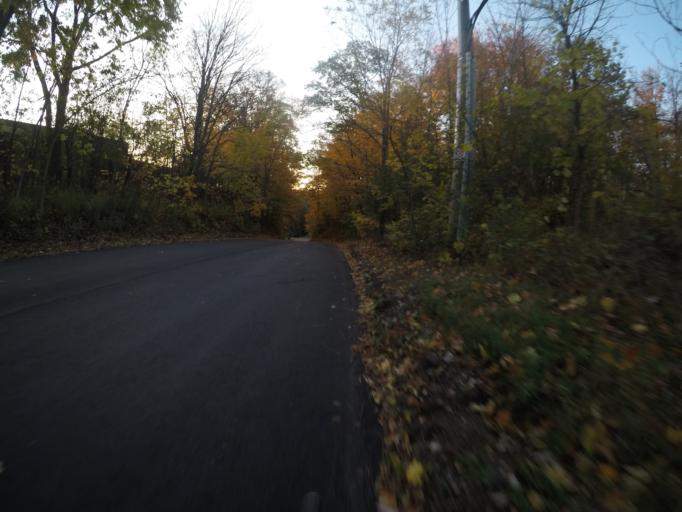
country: CA
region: Ontario
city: Kitchener
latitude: 43.4078
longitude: -80.4394
